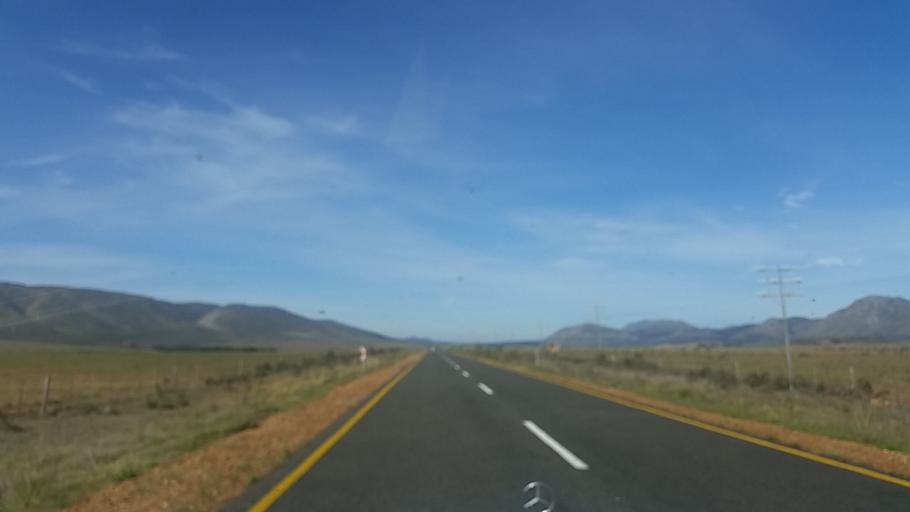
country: ZA
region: Western Cape
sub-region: Eden District Municipality
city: George
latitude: -33.8124
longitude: 22.5325
